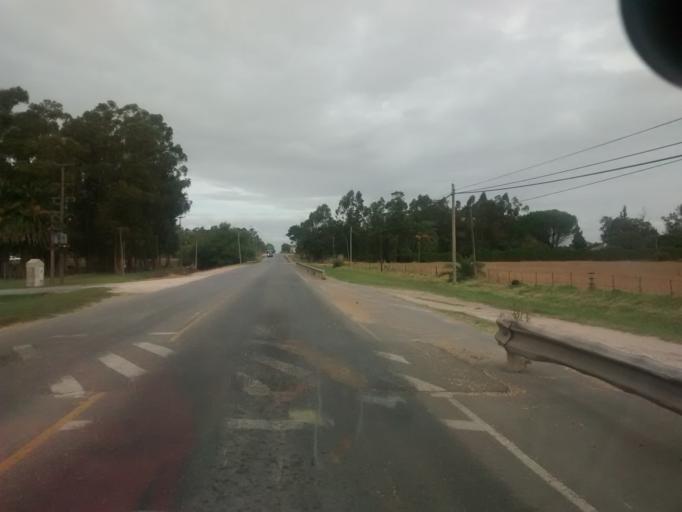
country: AR
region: Buenos Aires
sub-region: Partido de Loberia
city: Loberia
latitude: -38.1910
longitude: -58.7469
